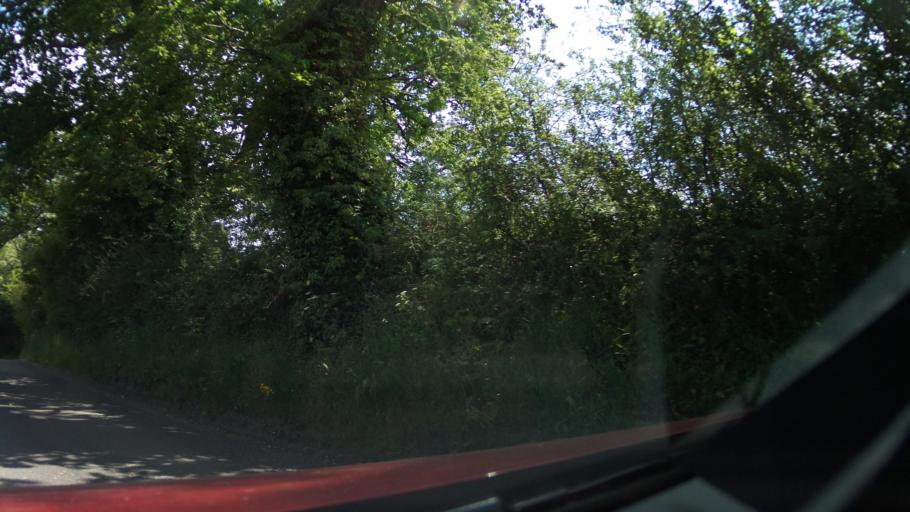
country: GB
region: England
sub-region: Wiltshire
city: Pewsey
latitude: 51.3427
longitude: -1.7794
